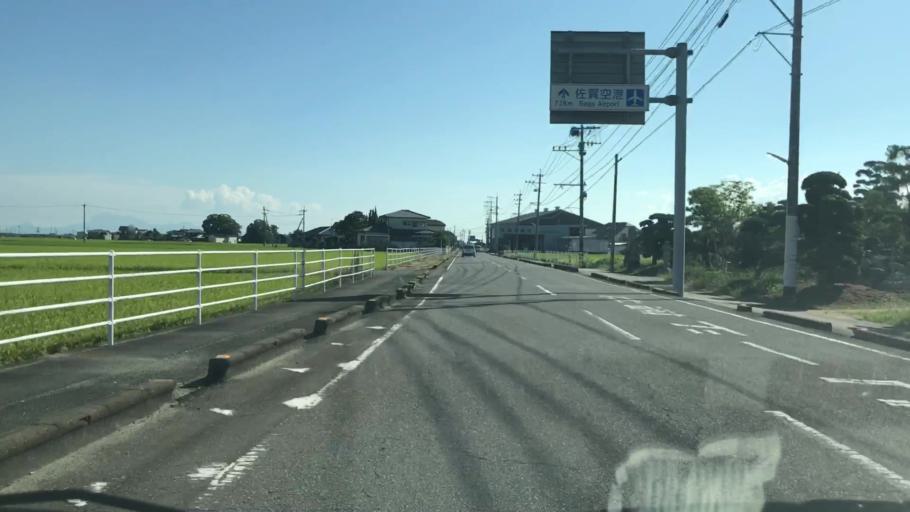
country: JP
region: Saga Prefecture
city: Okawa
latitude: 33.1956
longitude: 130.3346
